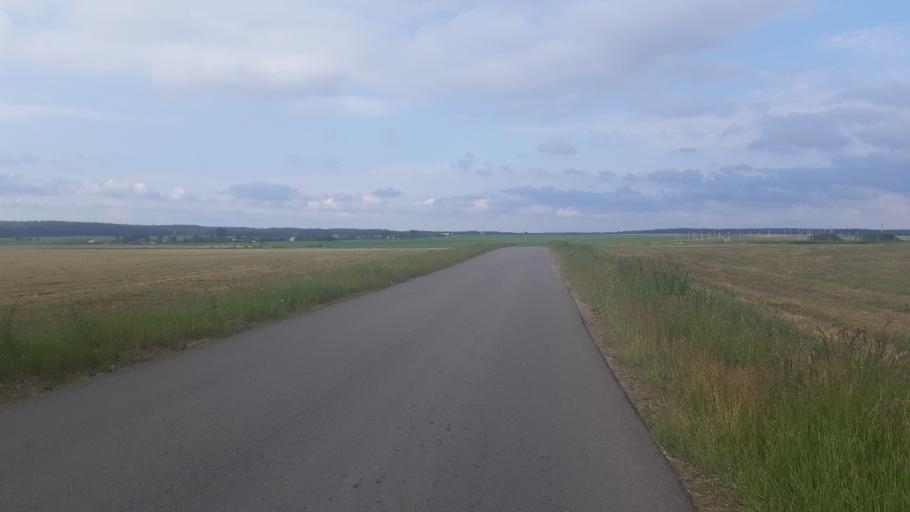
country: BY
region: Minsk
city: Horad Zhodzina
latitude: 54.1427
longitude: 28.2347
